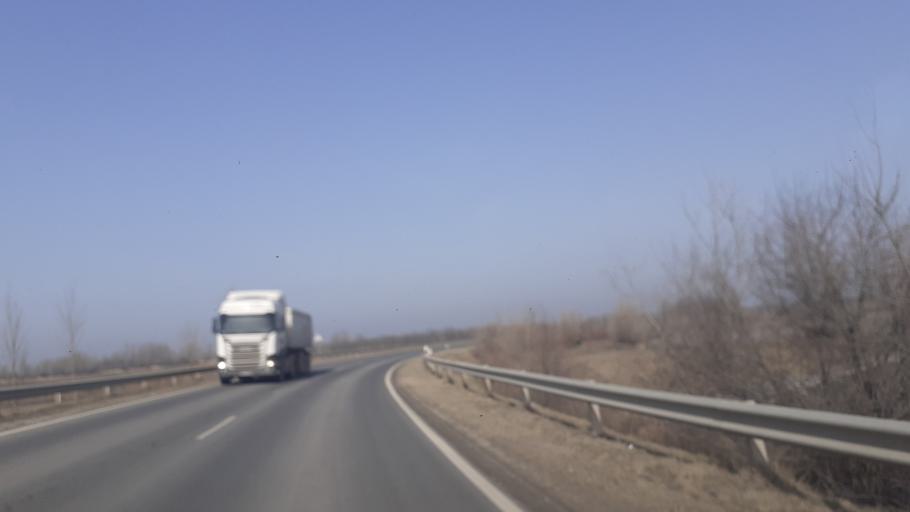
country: HU
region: Pest
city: Delegyhaza
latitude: 47.2308
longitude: 19.1162
